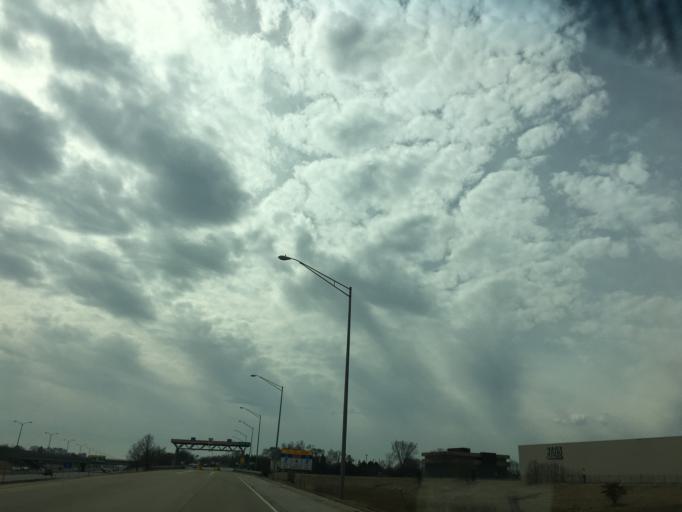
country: US
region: Illinois
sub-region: DuPage County
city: Woodridge
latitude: 41.7543
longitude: -88.0359
